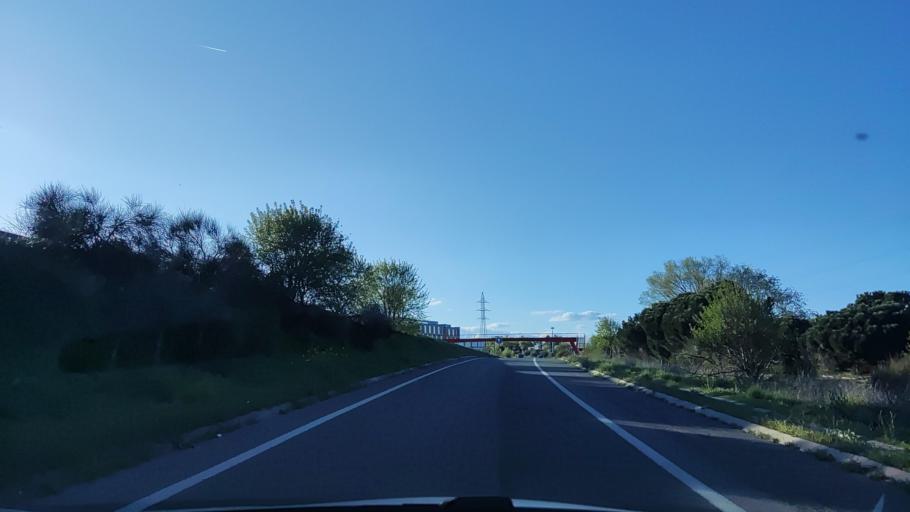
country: ES
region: Madrid
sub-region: Provincia de Madrid
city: Latina
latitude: 40.4010
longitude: -3.7793
